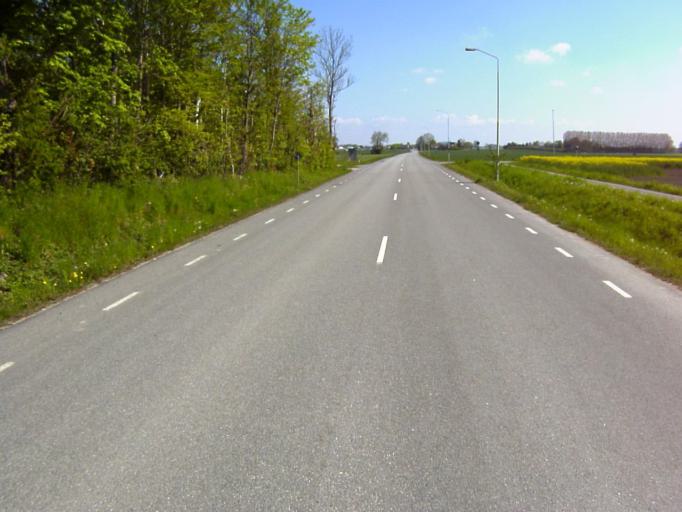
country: SE
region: Skane
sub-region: Kristianstads Kommun
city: Kristianstad
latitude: 56.0180
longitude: 14.2017
